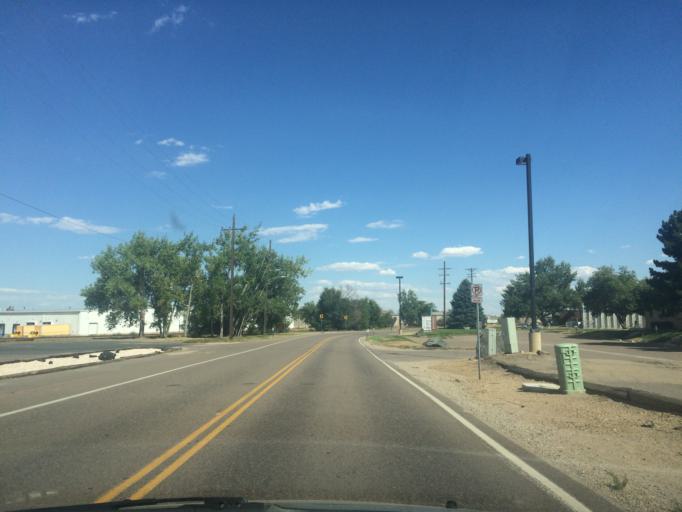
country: US
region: Colorado
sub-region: Broomfield County
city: Broomfield
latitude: 39.9214
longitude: -105.0989
